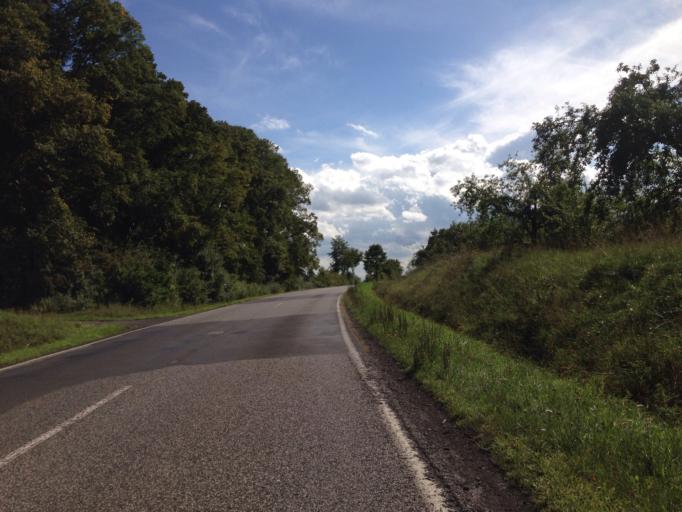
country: DE
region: Hesse
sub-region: Regierungsbezirk Giessen
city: Hungen
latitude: 50.4856
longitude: 8.9020
